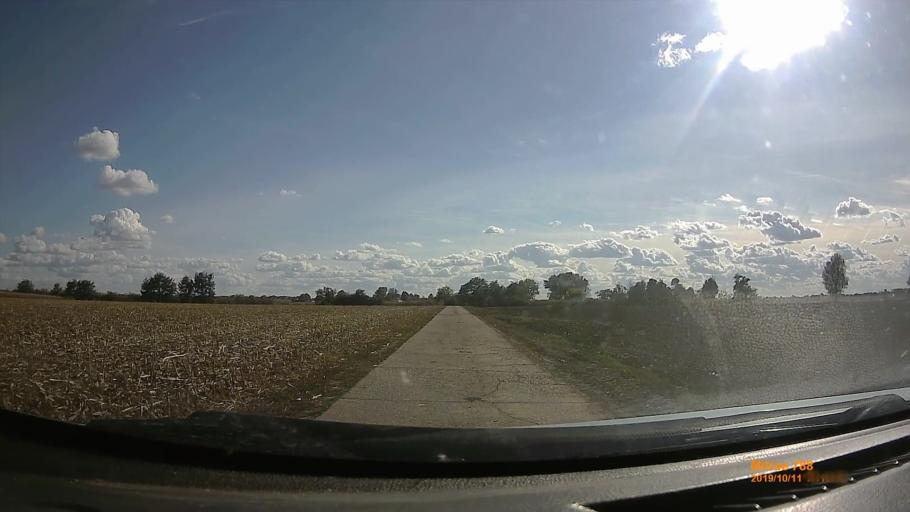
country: HU
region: Hajdu-Bihar
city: Hajduszoboszlo
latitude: 47.5316
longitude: 21.4016
